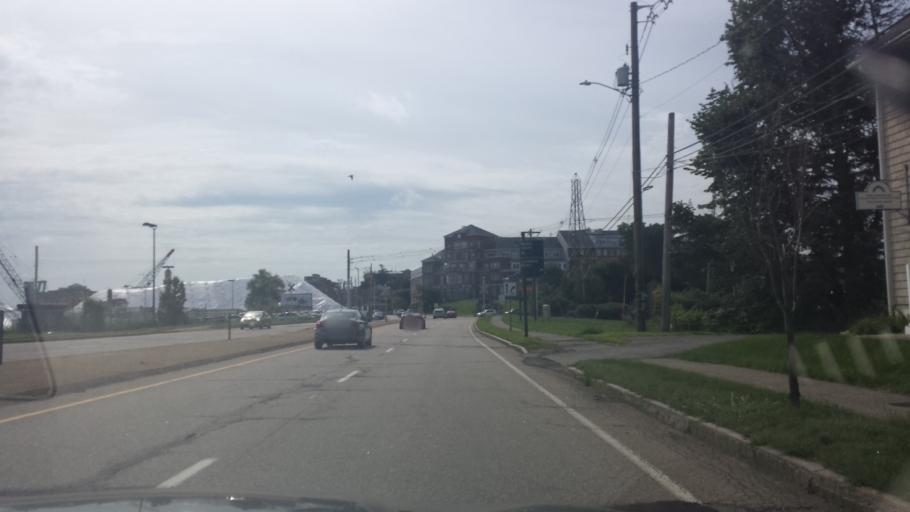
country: US
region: New Hampshire
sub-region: Rockingham County
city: Portsmouth
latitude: 43.0819
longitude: -70.7621
